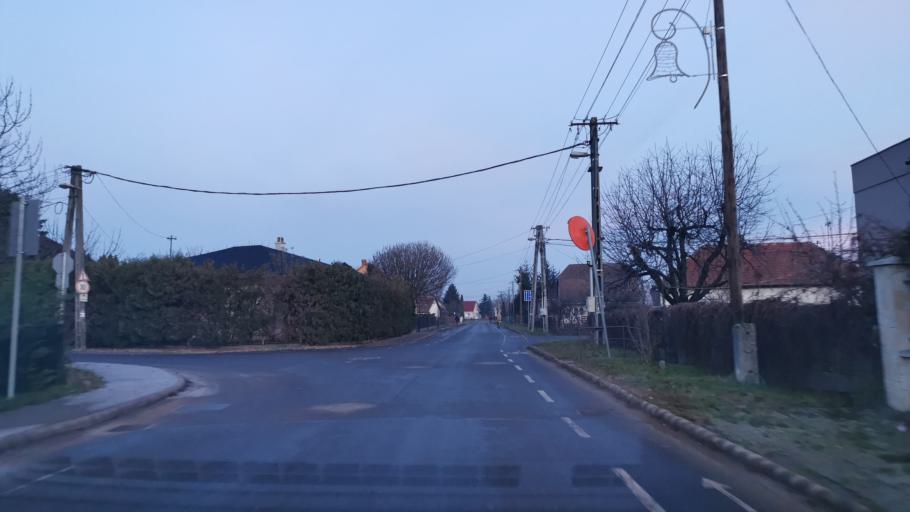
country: HU
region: Hajdu-Bihar
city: Hajduboszormeny
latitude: 47.5942
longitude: 21.5622
